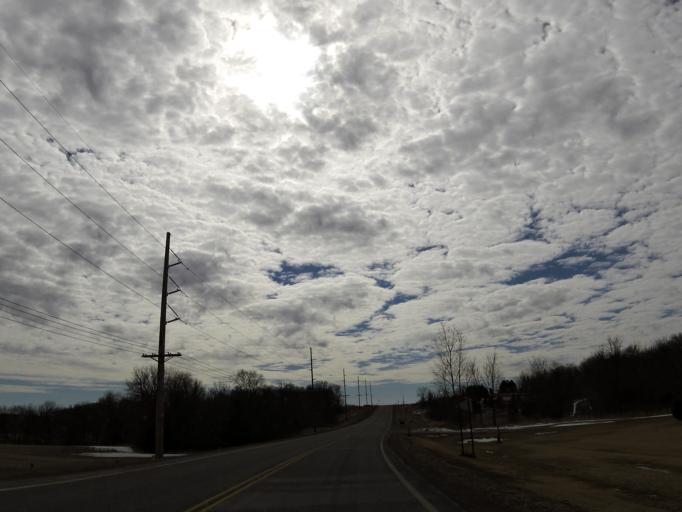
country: US
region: Minnesota
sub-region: Le Sueur County
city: New Prague
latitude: 44.6179
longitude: -93.5576
